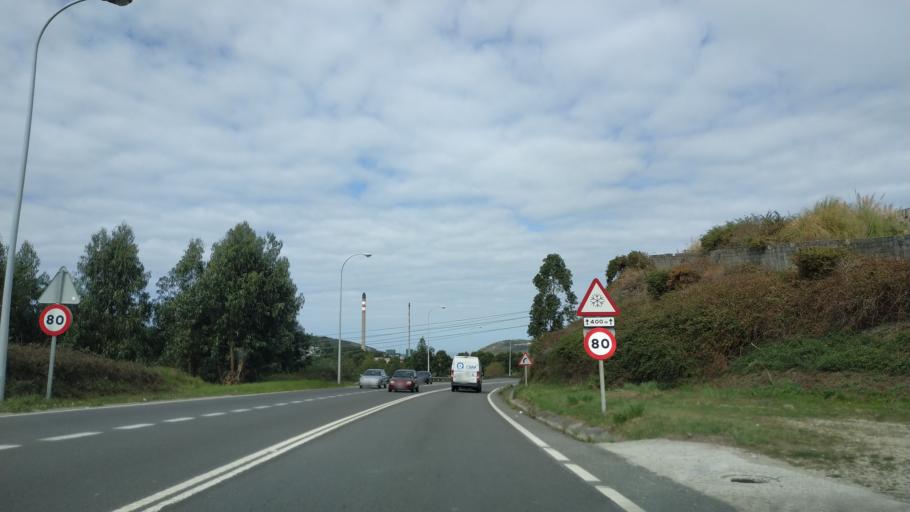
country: ES
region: Galicia
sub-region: Provincia da Coruna
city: Arteixo
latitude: 43.3363
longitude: -8.4544
